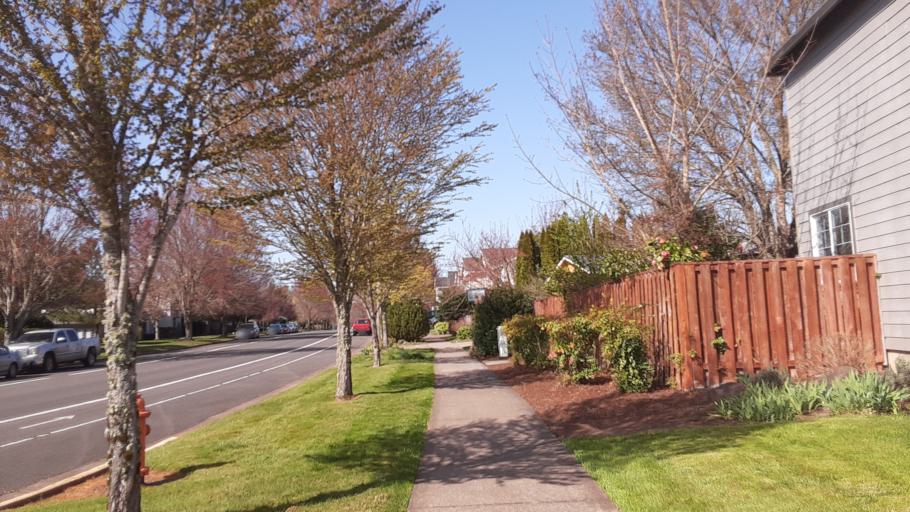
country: US
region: Oregon
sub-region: Benton County
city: Corvallis
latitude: 44.5319
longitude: -123.2565
